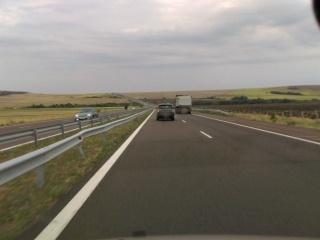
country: BG
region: Burgas
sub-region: Obshtina Karnobat
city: Karnobat
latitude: 42.5884
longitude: 27.0825
